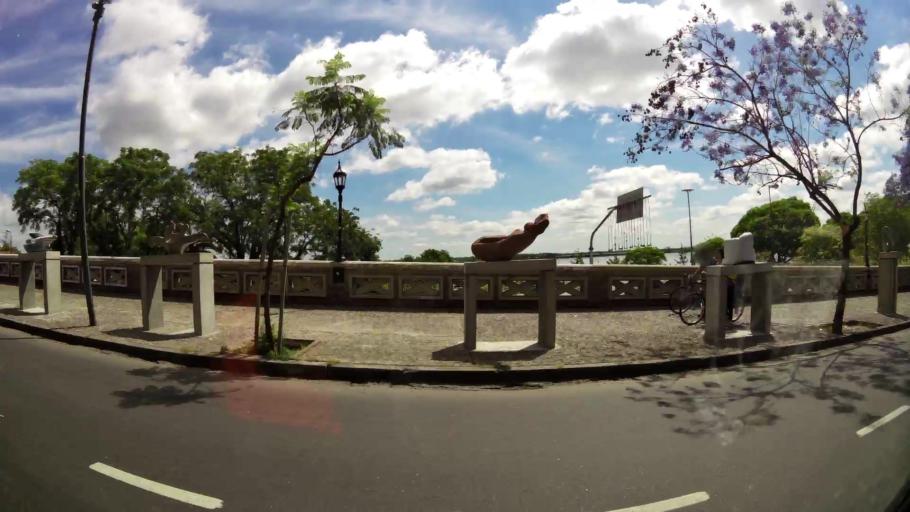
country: AR
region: Santa Fe
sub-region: Departamento de Rosario
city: Rosario
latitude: -32.9405
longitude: -60.6357
